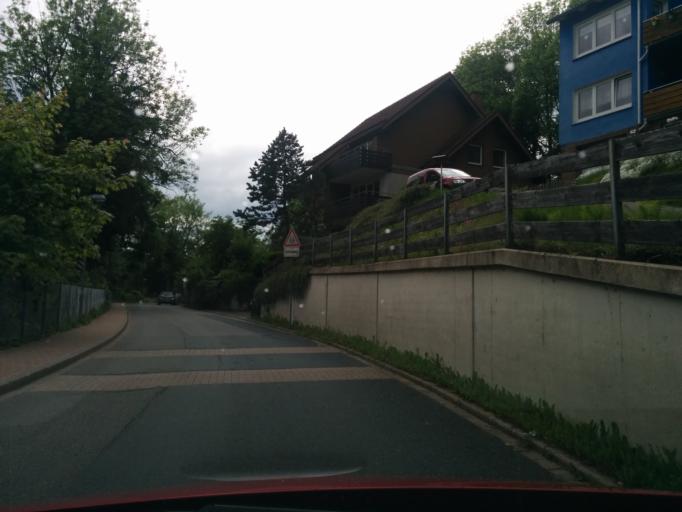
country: DE
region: Lower Saxony
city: Sankt Andreasberg
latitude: 51.7124
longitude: 10.5185
